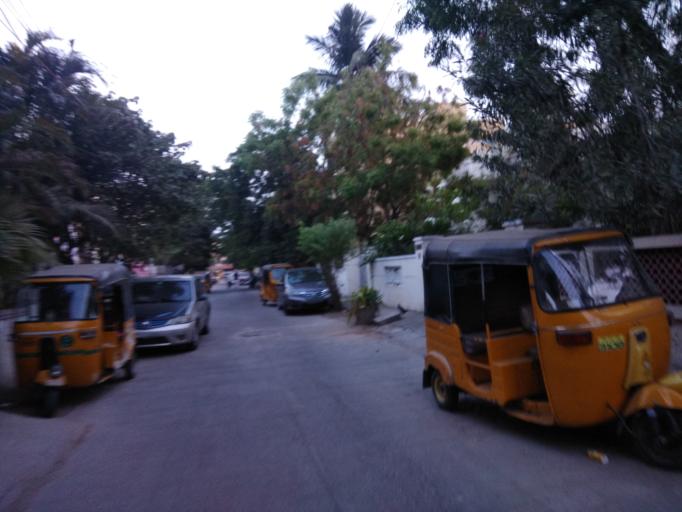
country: IN
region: Tamil Nadu
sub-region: Kancheepuram
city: Alandur
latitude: 13.0068
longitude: 80.2063
